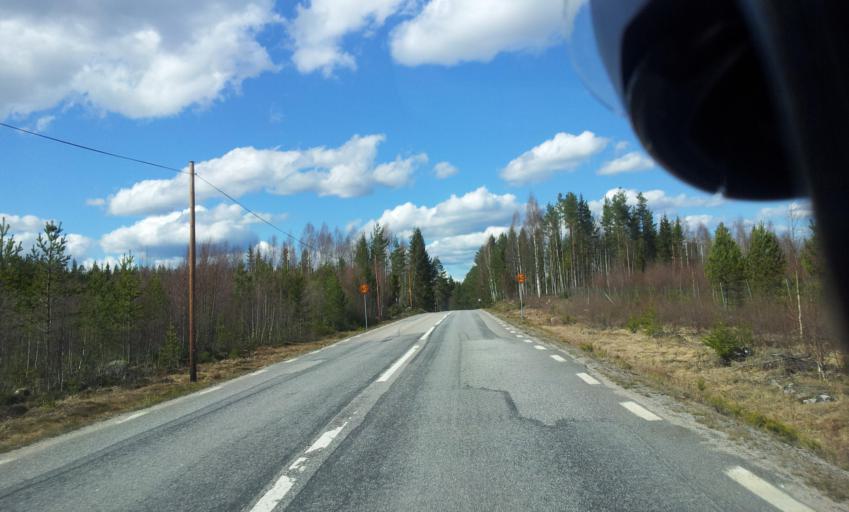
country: SE
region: Gaevleborg
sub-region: Ovanakers Kommun
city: Edsbyn
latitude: 61.3243
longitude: 15.8546
